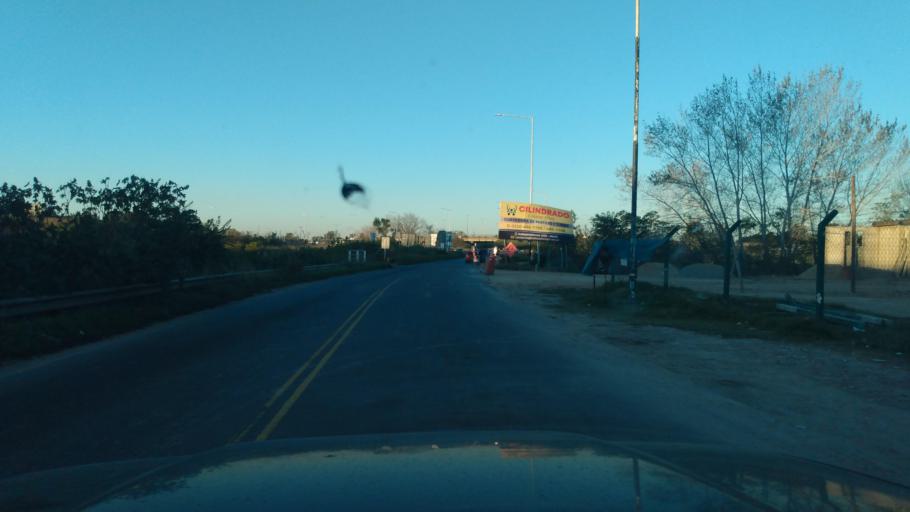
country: AR
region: Buenos Aires
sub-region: Partido de Merlo
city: Merlo
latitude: -34.6310
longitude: -58.7259
